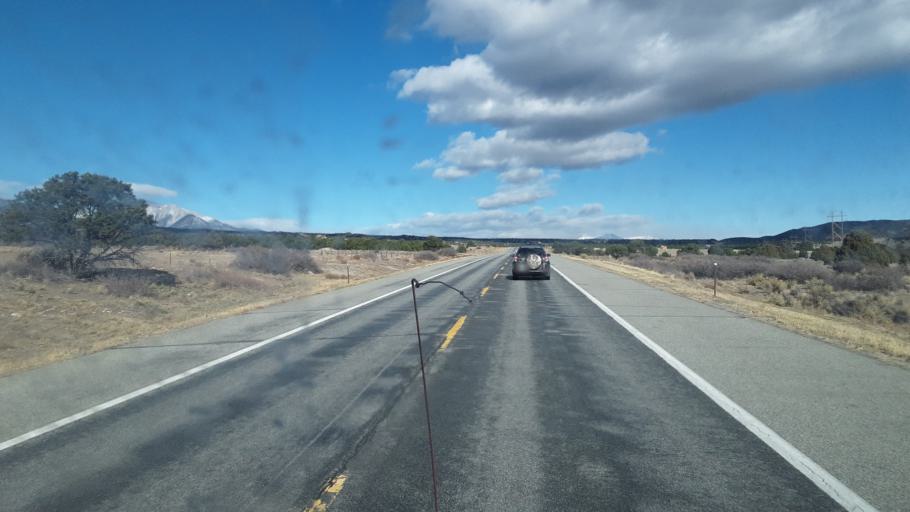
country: US
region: Colorado
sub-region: Chaffee County
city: Salida
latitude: 38.5854
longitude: -106.0832
